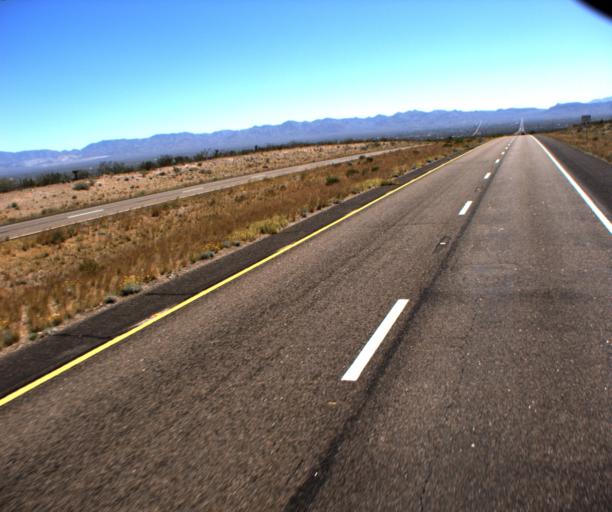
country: US
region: Arizona
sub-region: Mohave County
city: Golden Valley
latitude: 35.2281
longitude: -114.3448
